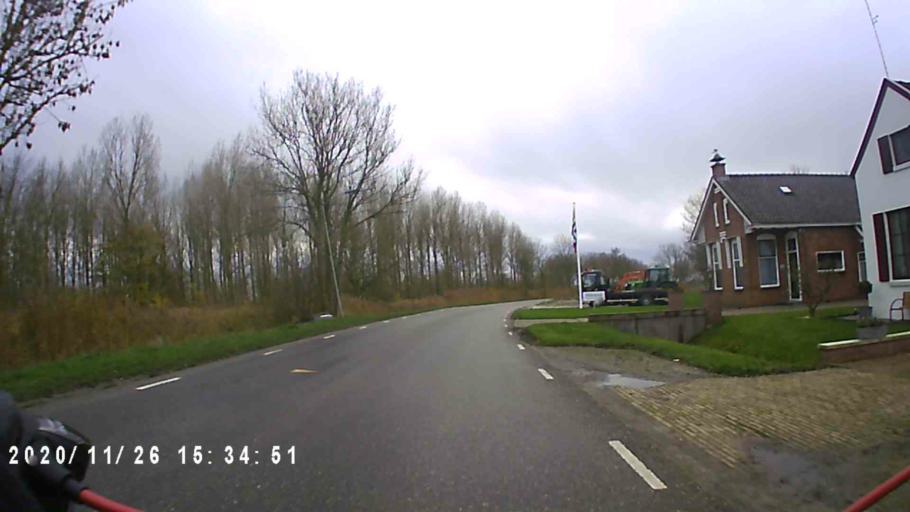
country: NL
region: Groningen
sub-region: Gemeente Slochteren
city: Slochteren
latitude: 53.3079
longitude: 6.7398
